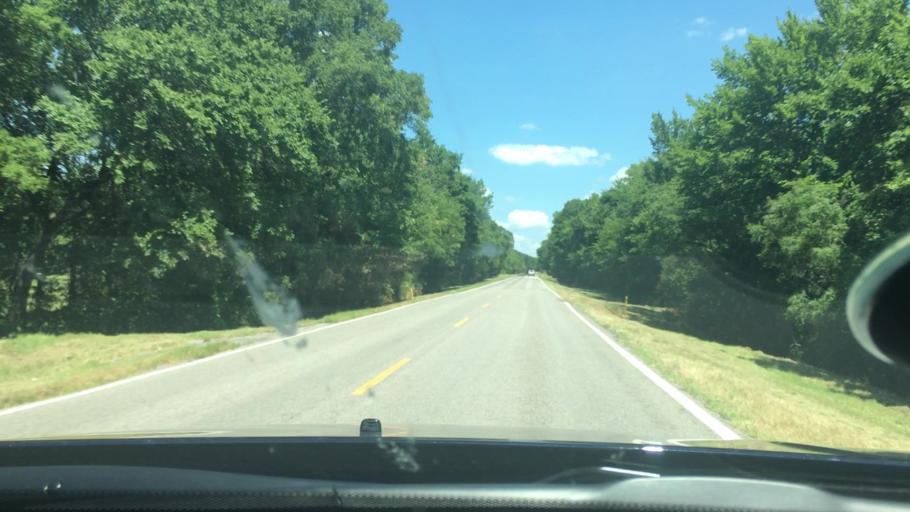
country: US
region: Oklahoma
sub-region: Carter County
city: Dickson
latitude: 34.3071
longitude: -96.9632
